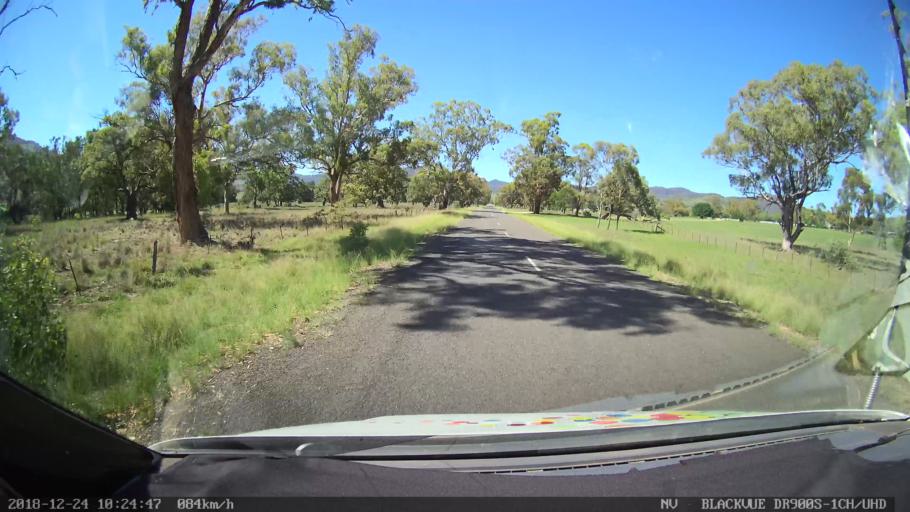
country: AU
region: New South Wales
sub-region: Liverpool Plains
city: Quirindi
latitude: -31.7907
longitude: 150.5313
